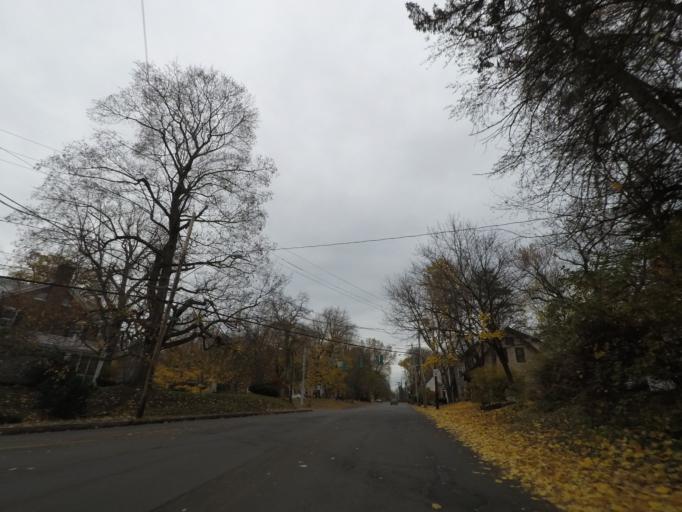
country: US
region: New York
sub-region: Rensselaer County
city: Troy
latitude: 42.7107
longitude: -73.6699
